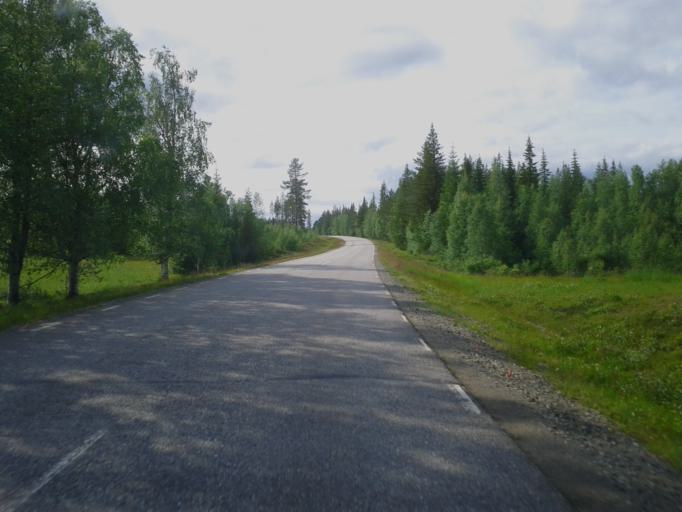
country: SE
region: Vaesterbotten
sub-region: Sorsele Kommun
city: Sorsele
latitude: 65.2848
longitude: 17.8564
